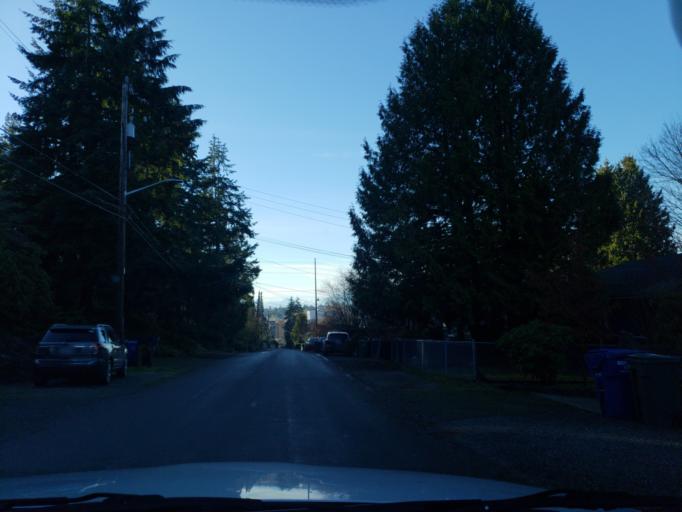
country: US
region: Washington
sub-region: King County
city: Shoreline
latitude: 47.7022
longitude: -122.3185
